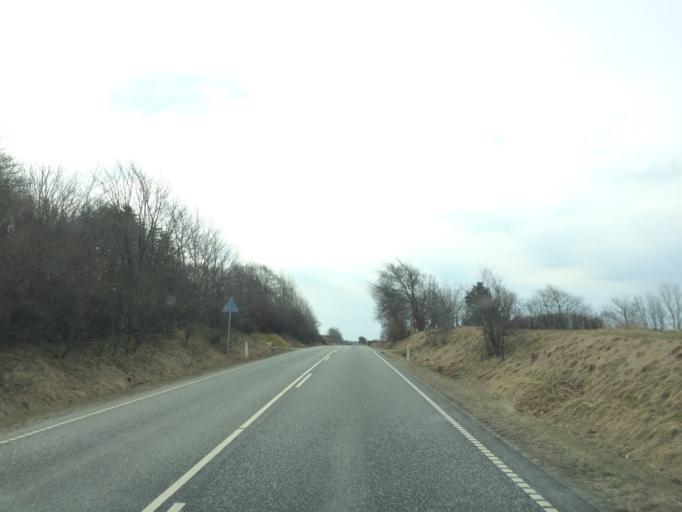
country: DK
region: Central Jutland
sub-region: Ringkobing-Skjern Kommune
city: Videbaek
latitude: 56.1051
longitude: 8.5078
